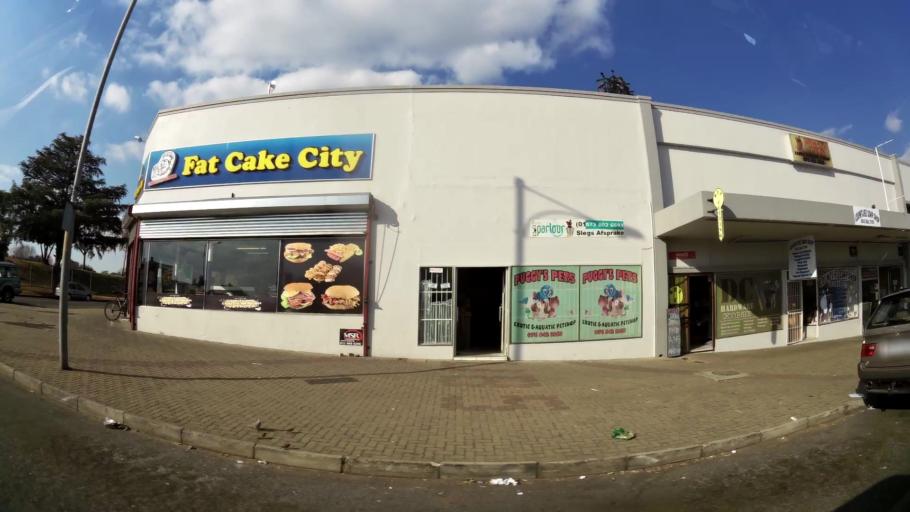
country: ZA
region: Gauteng
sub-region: West Rand District Municipality
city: Krugersdorp
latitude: -26.0915
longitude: 27.7687
